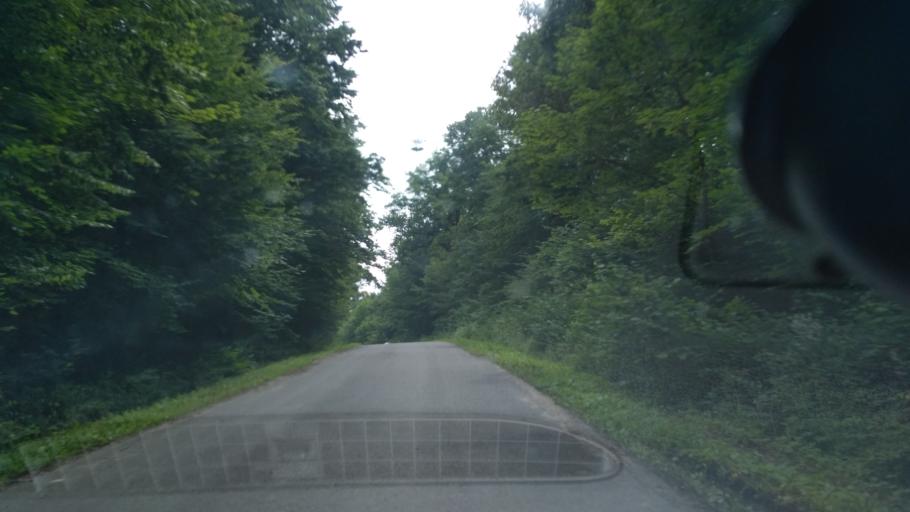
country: PL
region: Subcarpathian Voivodeship
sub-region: Powiat przeworski
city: Lopuszka Wielka
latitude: 49.9071
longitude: 22.3998
